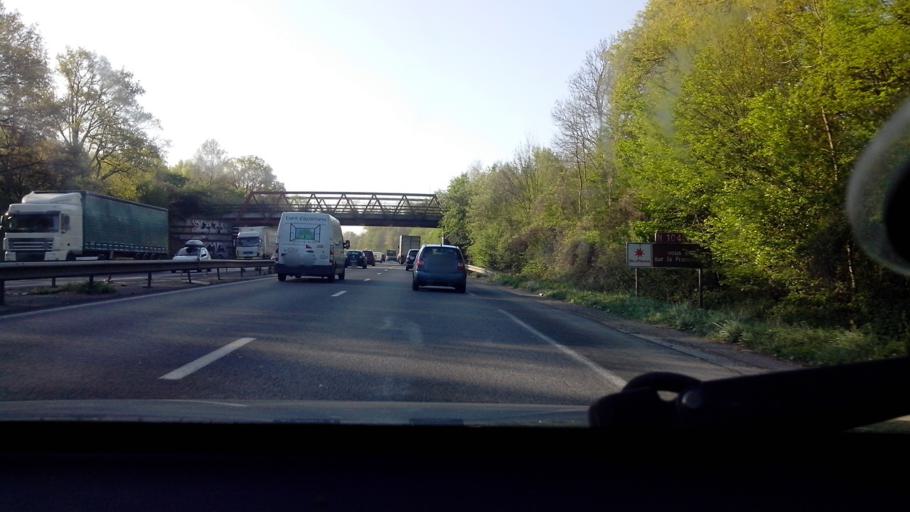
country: FR
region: Ile-de-France
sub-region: Departement de Seine-et-Marne
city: Lesigny
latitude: 48.7692
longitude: 2.6126
